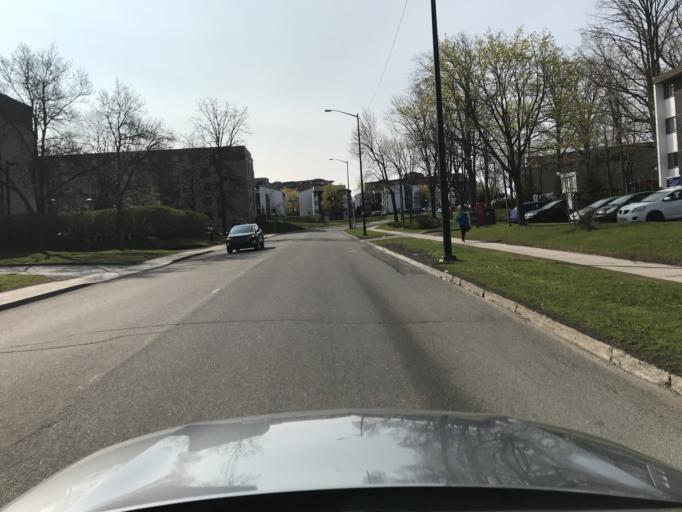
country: CA
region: Quebec
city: L'Ancienne-Lorette
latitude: 46.7900
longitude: -71.2831
